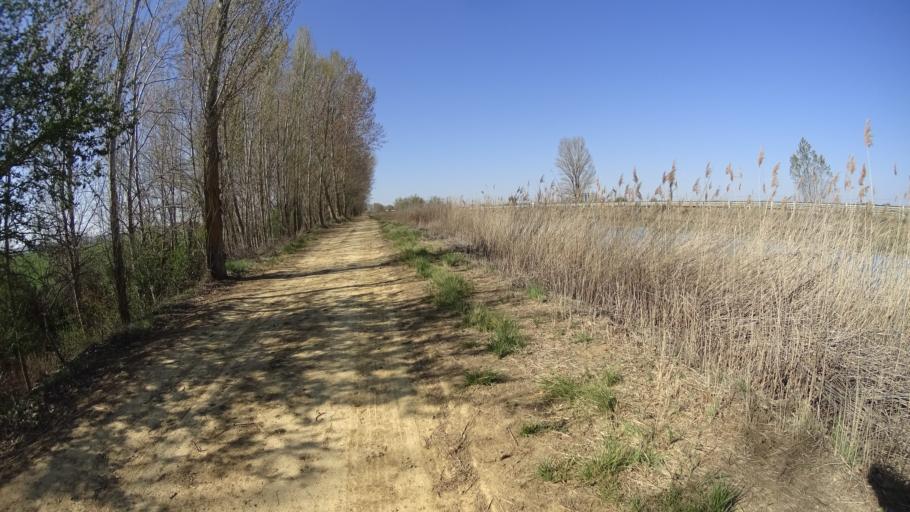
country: ES
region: Castille and Leon
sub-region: Provincia de Palencia
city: Fromista
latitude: 42.2545
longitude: -4.4110
